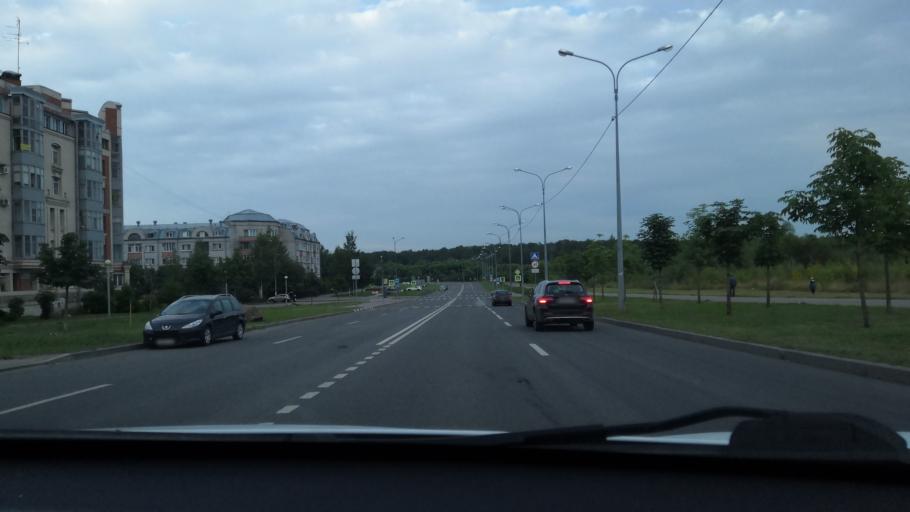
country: RU
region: St.-Petersburg
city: Pavlovsk
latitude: 59.6940
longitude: 30.4229
